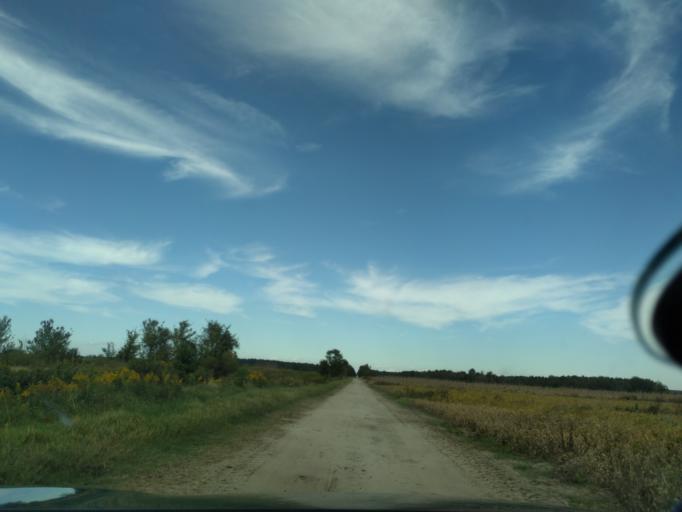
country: US
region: North Carolina
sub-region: Beaufort County
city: Belhaven
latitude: 35.7072
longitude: -76.5865
